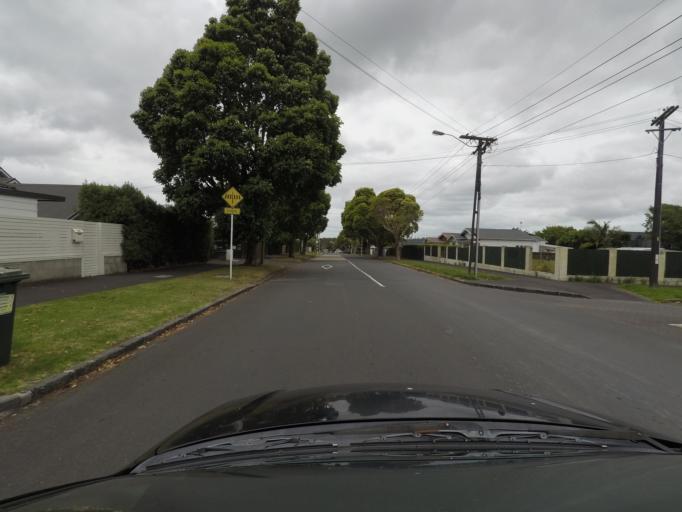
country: NZ
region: Auckland
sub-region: Auckland
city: Rosebank
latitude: -36.8629
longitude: 174.7071
